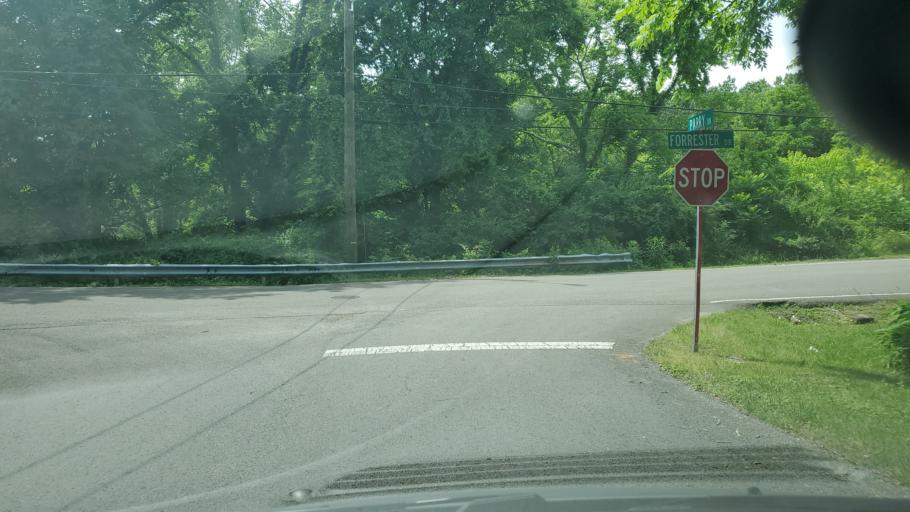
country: US
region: Tennessee
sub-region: Davidson County
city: Oak Hill
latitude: 36.1058
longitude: -86.6955
